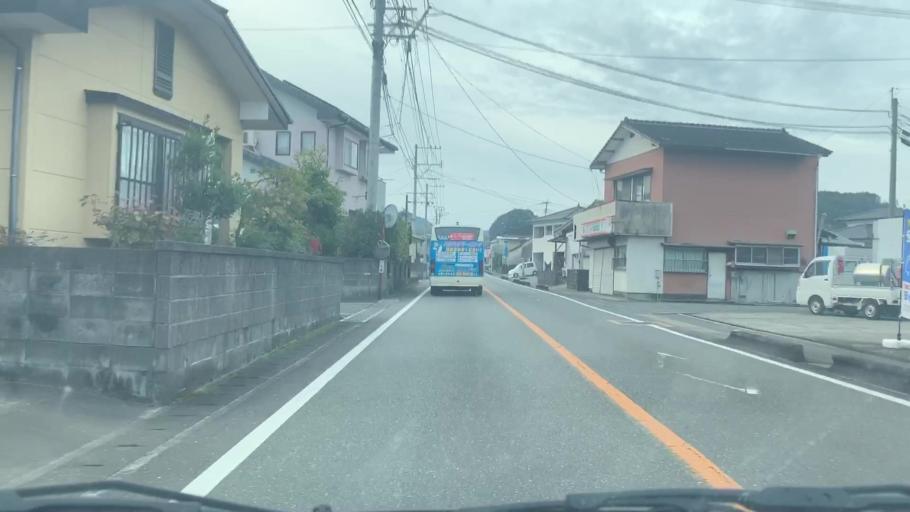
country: JP
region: Saga Prefecture
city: Ureshinomachi-shimojuku
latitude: 33.1242
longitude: 130.0028
